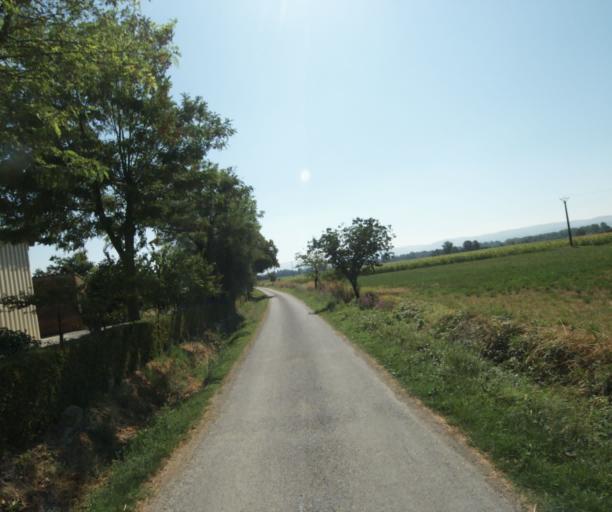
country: FR
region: Midi-Pyrenees
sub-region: Departement de la Haute-Garonne
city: Revel
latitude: 43.5079
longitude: 1.9514
